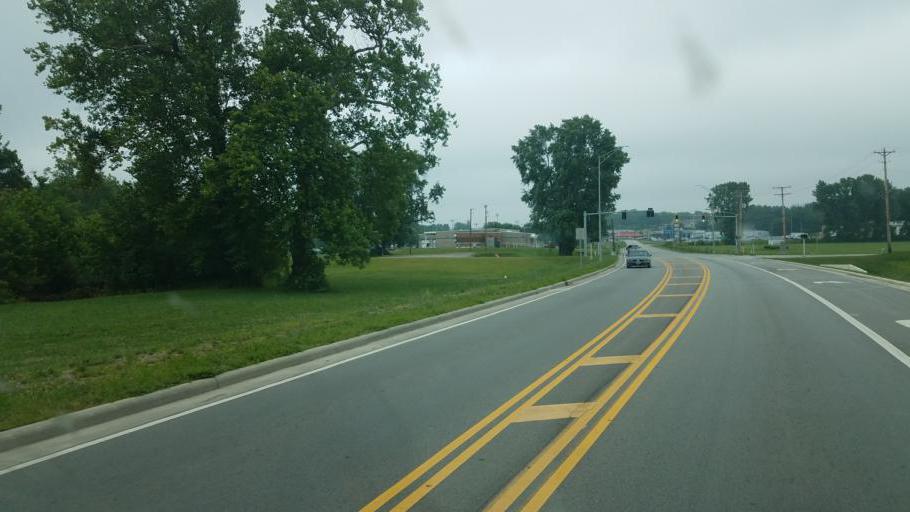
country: US
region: Ohio
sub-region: Highland County
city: Hillsboro
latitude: 39.2358
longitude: -83.6094
